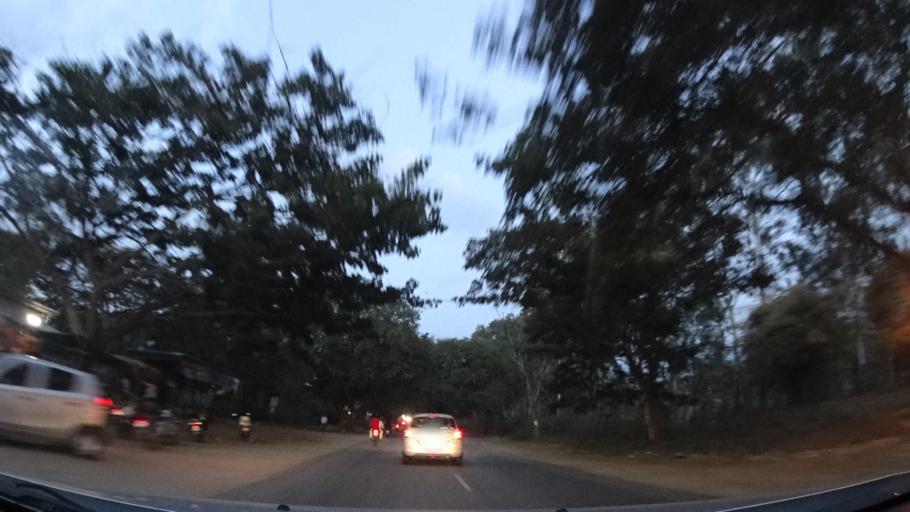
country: IN
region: Karnataka
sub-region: Bangalore Urban
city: Anekal
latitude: 12.7858
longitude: 77.5023
